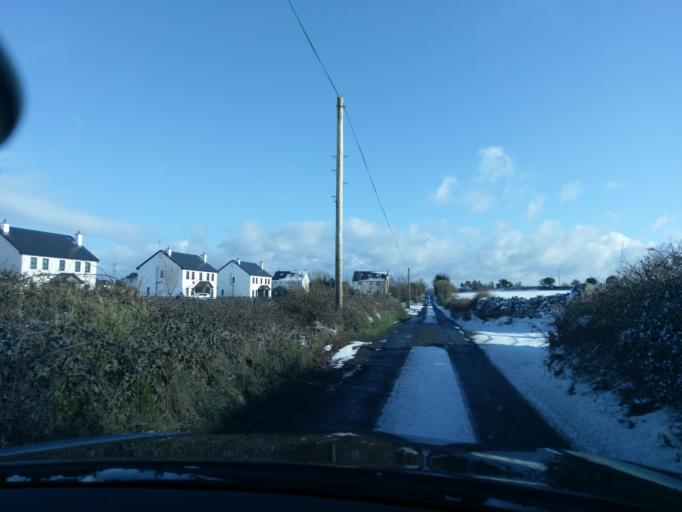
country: IE
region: Connaught
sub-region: County Galway
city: Athenry
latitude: 53.1933
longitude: -8.7938
